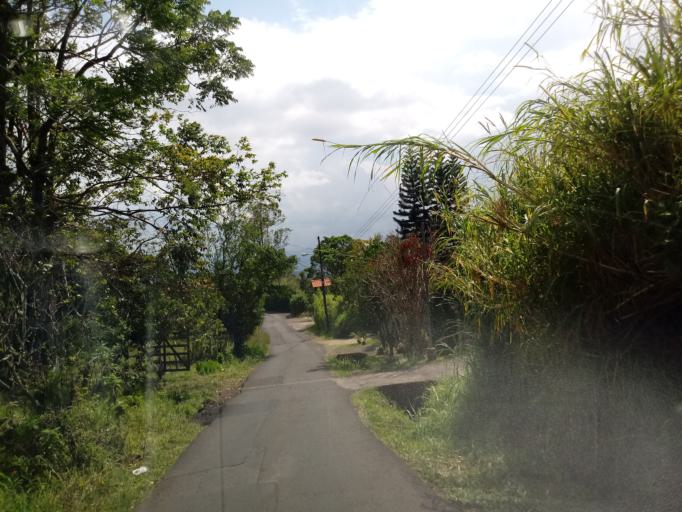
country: CR
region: Heredia
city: Angeles
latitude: 10.0282
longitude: -84.0317
